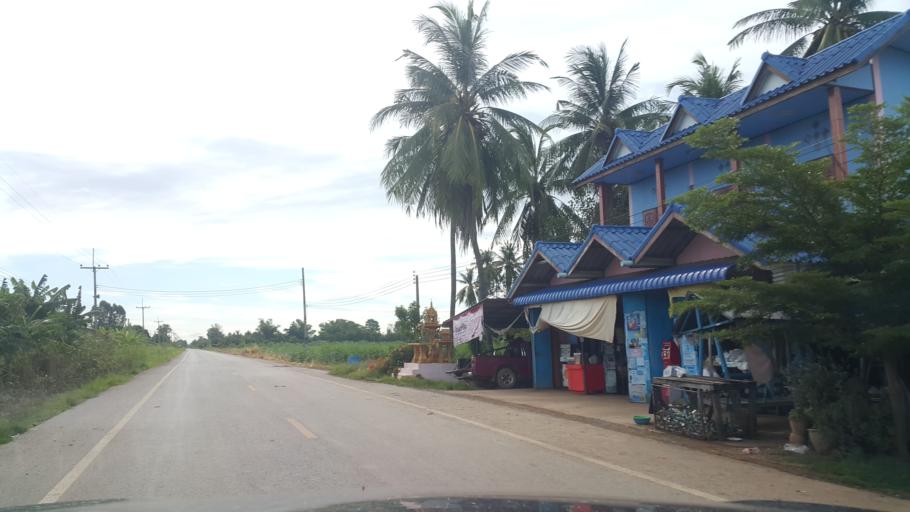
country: TH
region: Sukhothai
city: Si Nakhon
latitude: 17.2614
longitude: 99.9291
